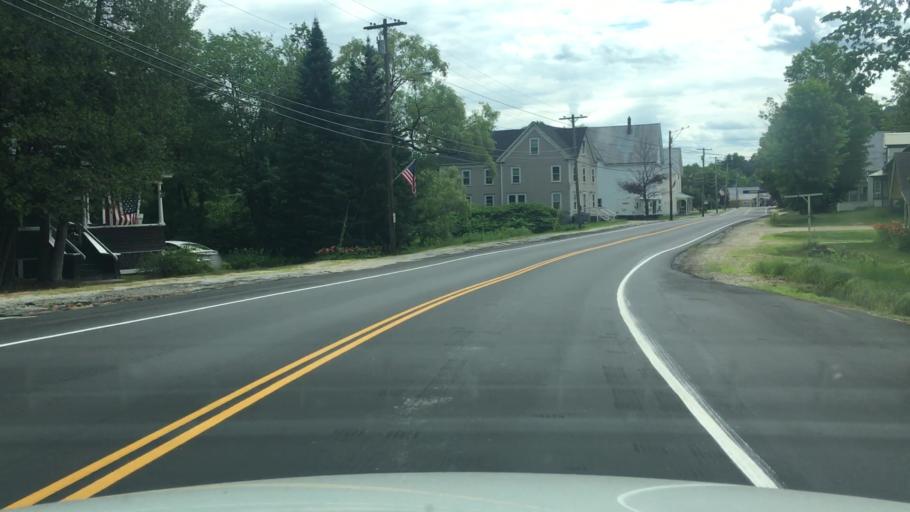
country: US
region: Maine
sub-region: Oxford County
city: West Paris
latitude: 44.3812
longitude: -70.6431
